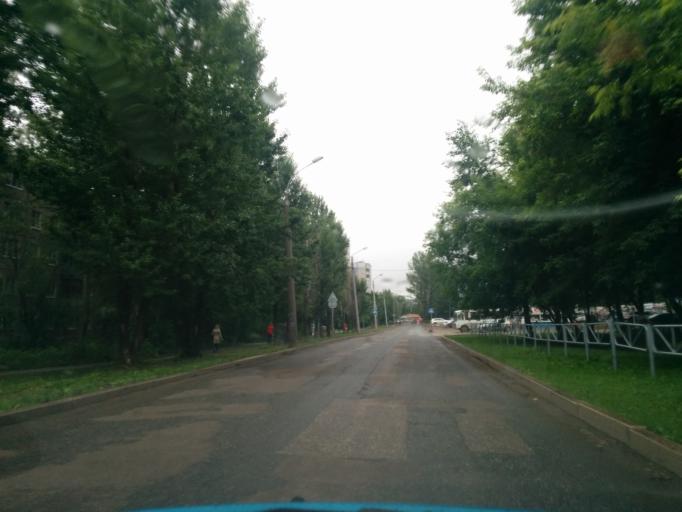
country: RU
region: Perm
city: Perm
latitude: 57.9922
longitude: 56.2310
